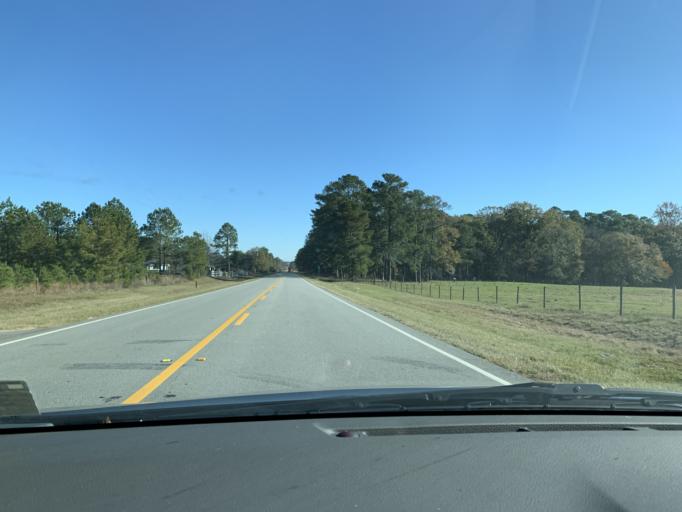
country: US
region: Georgia
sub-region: Ben Hill County
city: Fitzgerald
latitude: 31.7462
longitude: -83.1448
